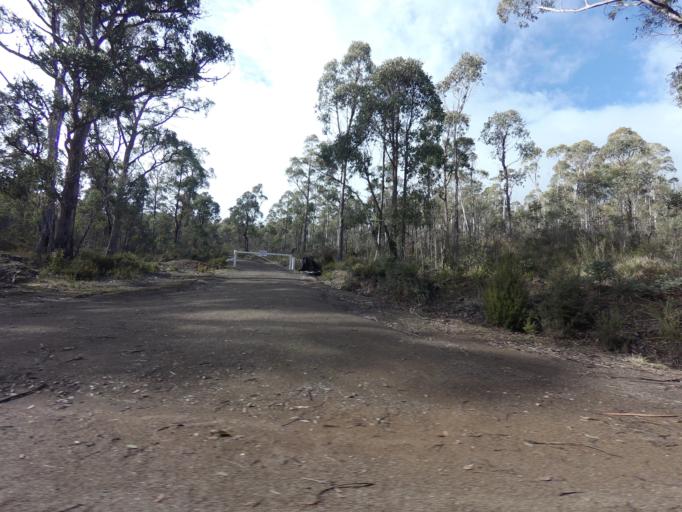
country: AU
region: Tasmania
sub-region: Derwent Valley
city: New Norfolk
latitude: -42.7701
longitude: 146.9003
